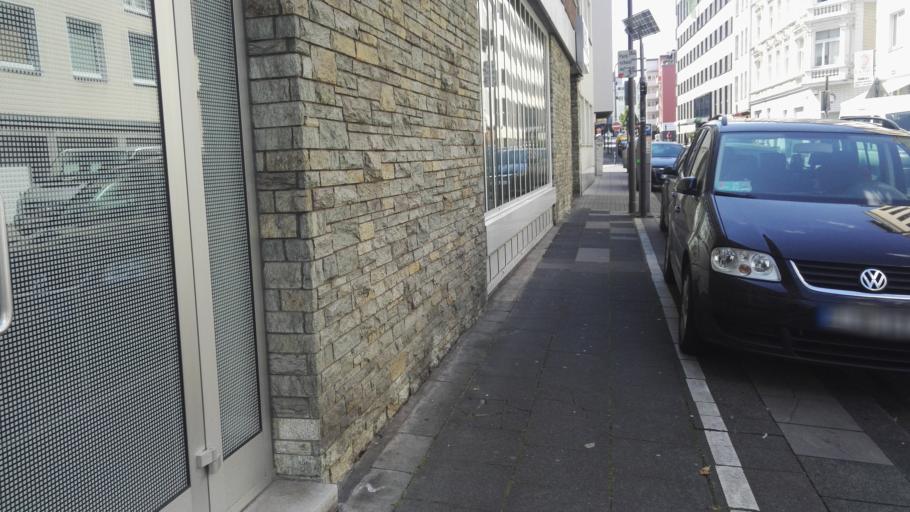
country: DE
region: North Rhine-Westphalia
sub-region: Regierungsbezirk Koln
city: Altstadt Nord
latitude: 50.9465
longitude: 6.9597
